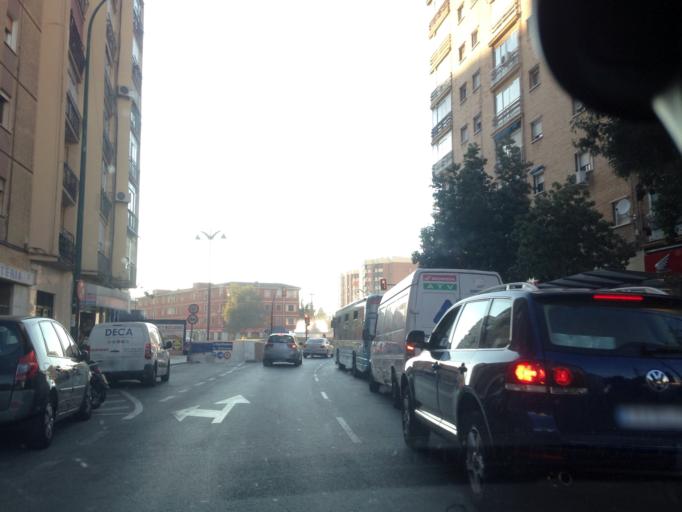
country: ES
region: Andalusia
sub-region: Provincia de Malaga
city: Malaga
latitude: 36.7122
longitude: -4.4399
